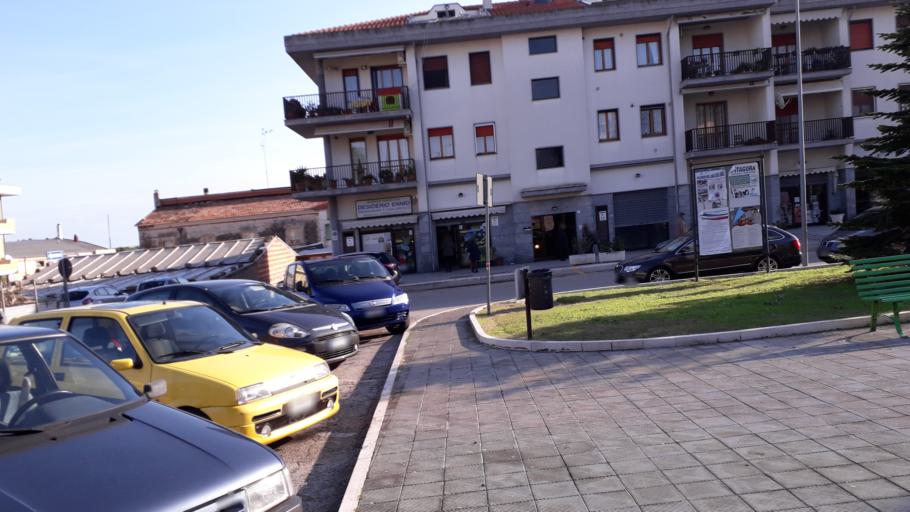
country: IT
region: Molise
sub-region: Provincia di Campobasso
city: Campomarino
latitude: 41.9543
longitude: 15.0340
